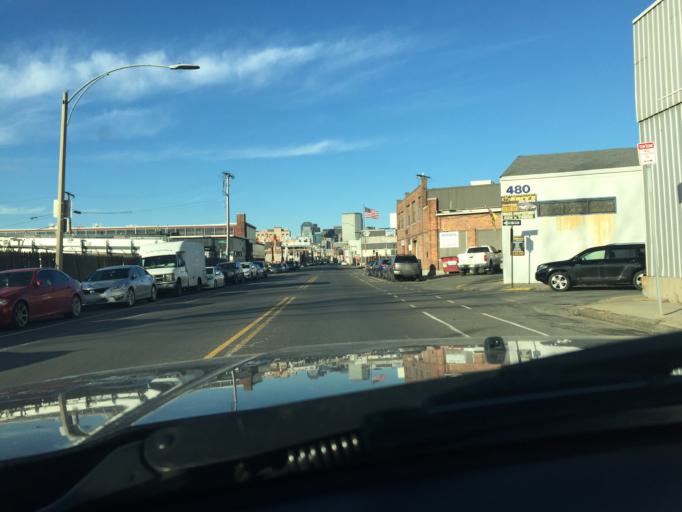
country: US
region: Massachusetts
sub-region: Suffolk County
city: South Boston
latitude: 42.3321
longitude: -71.0570
